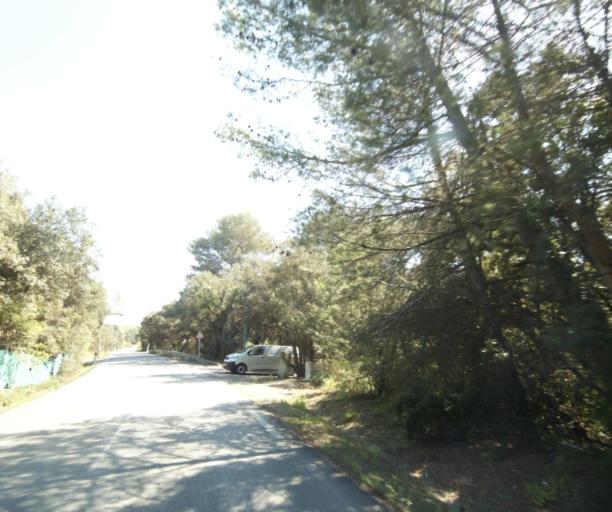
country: FR
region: Languedoc-Roussillon
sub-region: Departement de l'Herault
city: Sussargues
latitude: 43.7022
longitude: 4.0074
